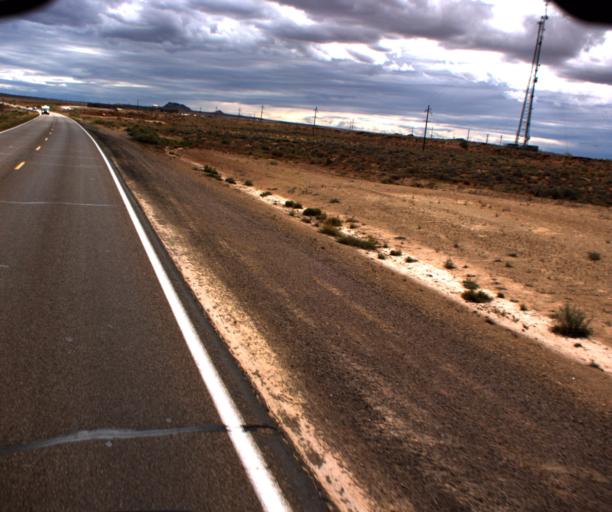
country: US
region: Arizona
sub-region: Navajo County
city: Holbrook
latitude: 34.8779
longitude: -110.1626
